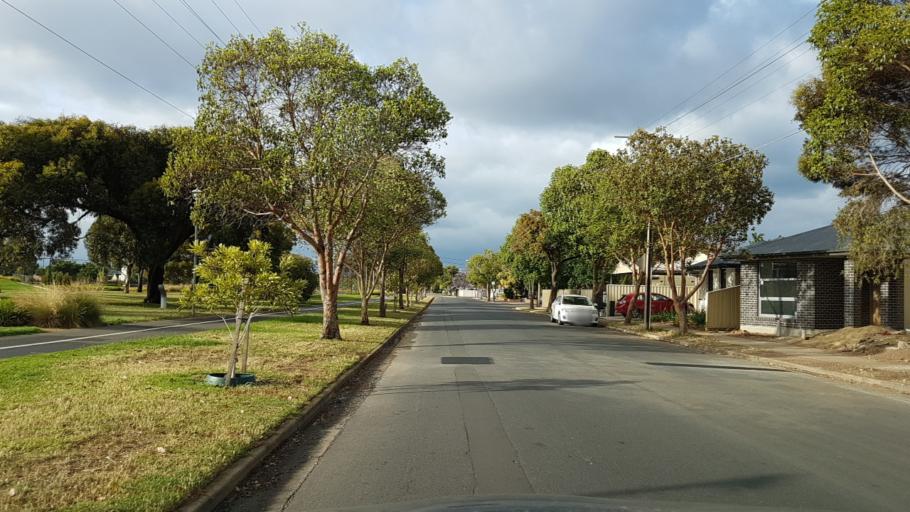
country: AU
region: South Australia
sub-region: City of West Torrens
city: Plympton
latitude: -34.9552
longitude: 138.5581
